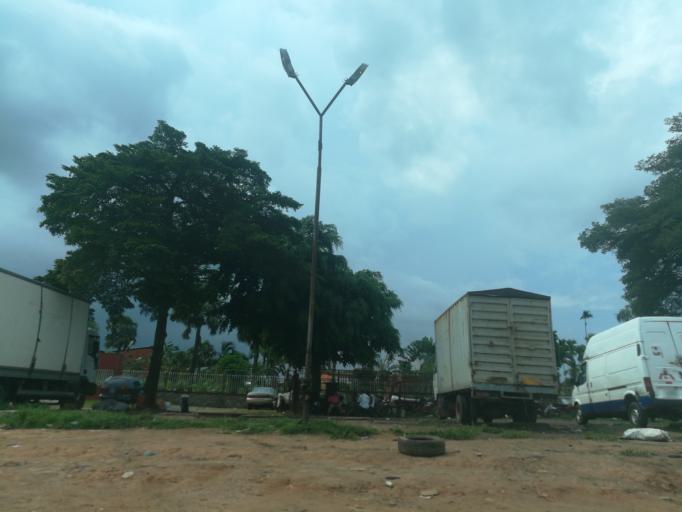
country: NG
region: Lagos
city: Ikorodu
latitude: 6.6403
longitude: 3.5484
